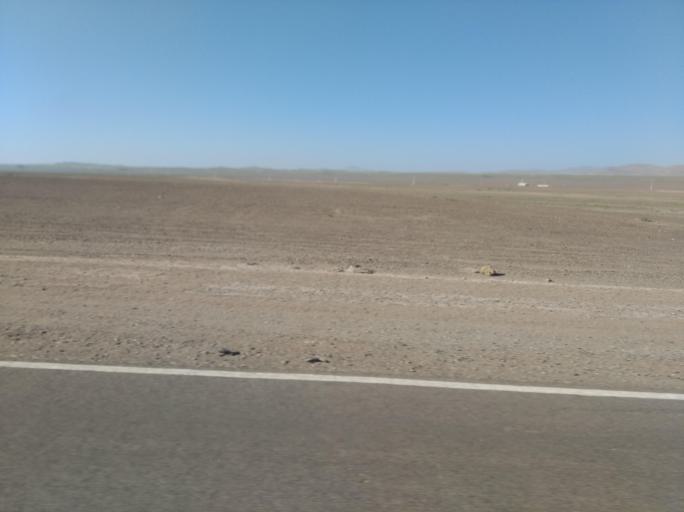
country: CL
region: Atacama
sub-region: Provincia de Copiapo
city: Copiapo
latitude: -27.3286
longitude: -70.7963
